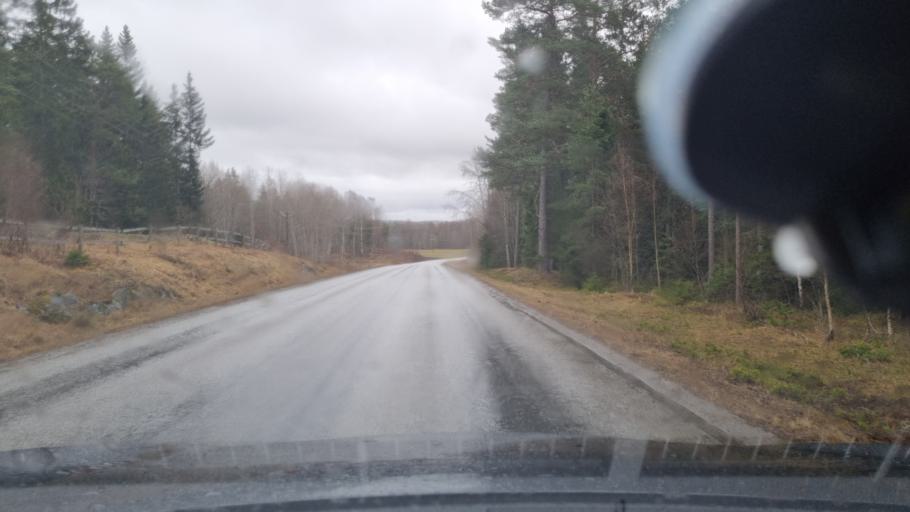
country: SE
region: Stockholm
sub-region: Sigtuna Kommun
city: Sigtuna
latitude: 59.5533
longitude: 17.7291
